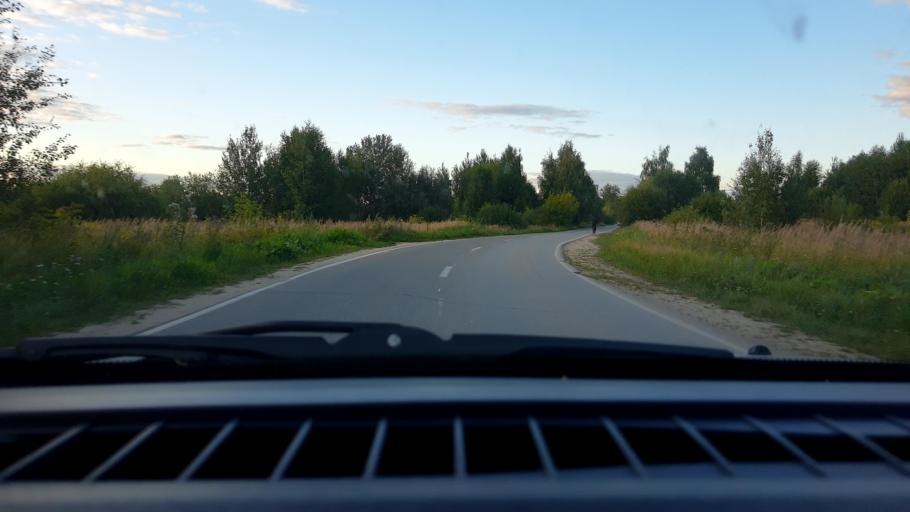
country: RU
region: Nizjnij Novgorod
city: Bor
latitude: 56.3440
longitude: 44.0468
